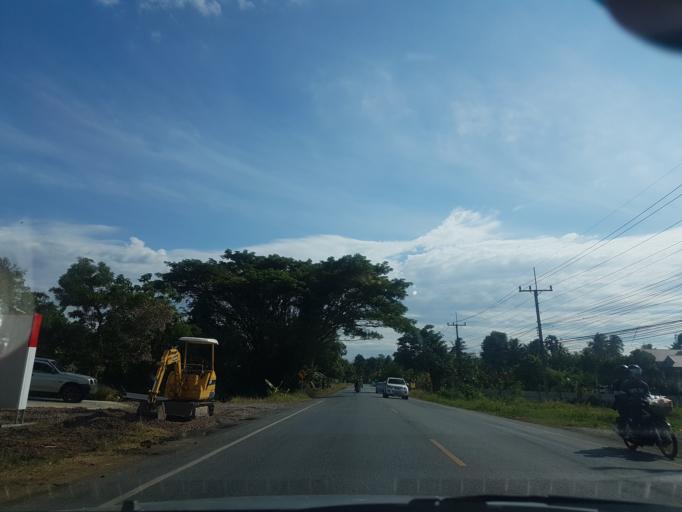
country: TH
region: Lop Buri
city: Lop Buri
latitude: 14.8013
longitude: 100.7402
